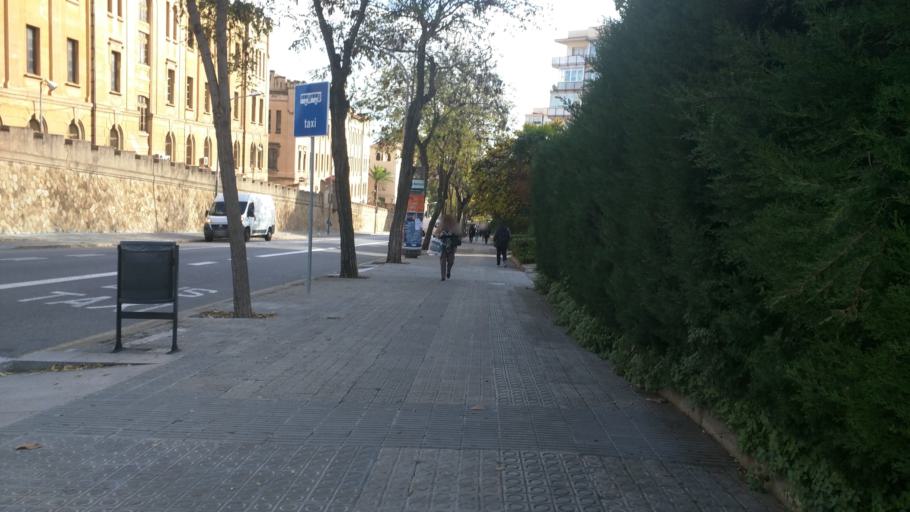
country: ES
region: Catalonia
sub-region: Provincia de Barcelona
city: Esplugues de Llobregat
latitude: 41.3861
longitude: 2.1080
